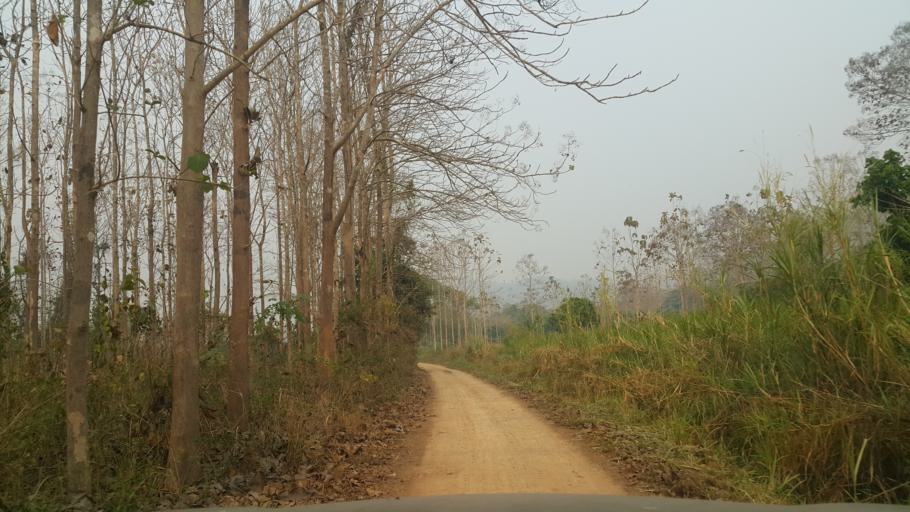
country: TH
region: Lamphun
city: Mae Tha
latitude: 18.5077
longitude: 99.2132
